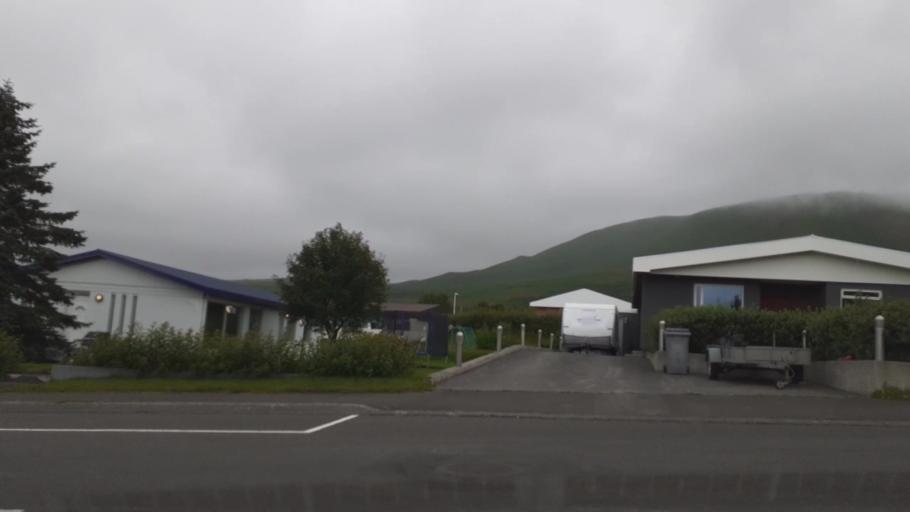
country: IS
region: Northeast
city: Husavik
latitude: 66.0394
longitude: -17.3359
